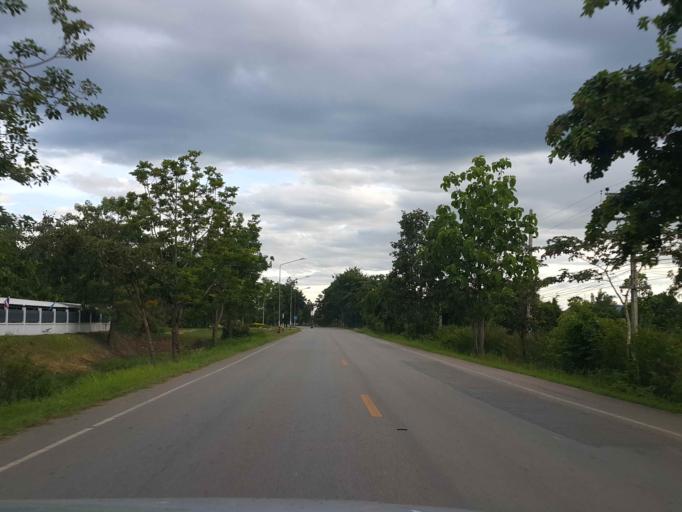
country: TH
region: Sukhothai
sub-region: Amphoe Si Satchanalai
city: Si Satchanalai
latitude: 17.4644
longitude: 99.7329
